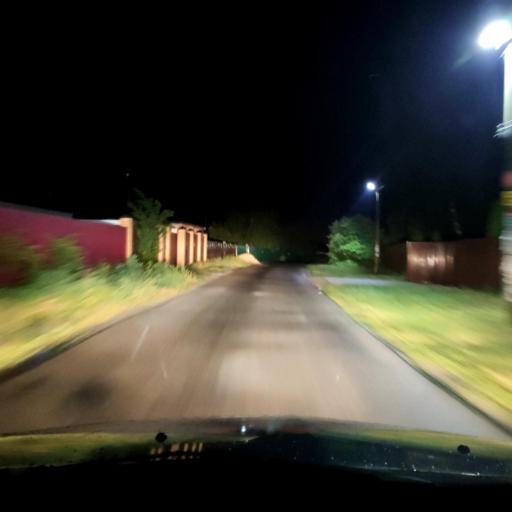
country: RU
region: Voronezj
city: Podkletnoye
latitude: 51.6184
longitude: 39.5311
